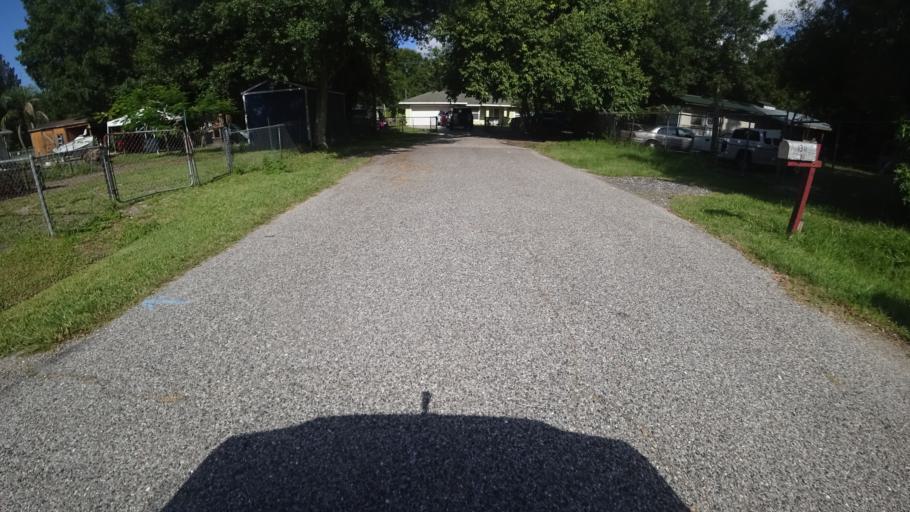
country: US
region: Florida
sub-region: Manatee County
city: Samoset
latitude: 27.4417
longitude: -82.5485
